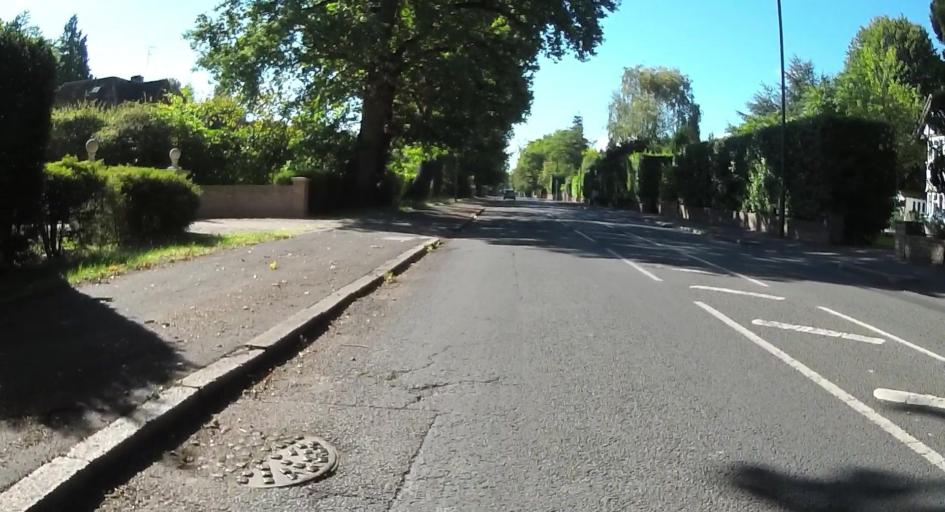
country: GB
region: England
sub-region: Surrey
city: Walton-on-Thames
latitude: 51.3790
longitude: -0.4194
